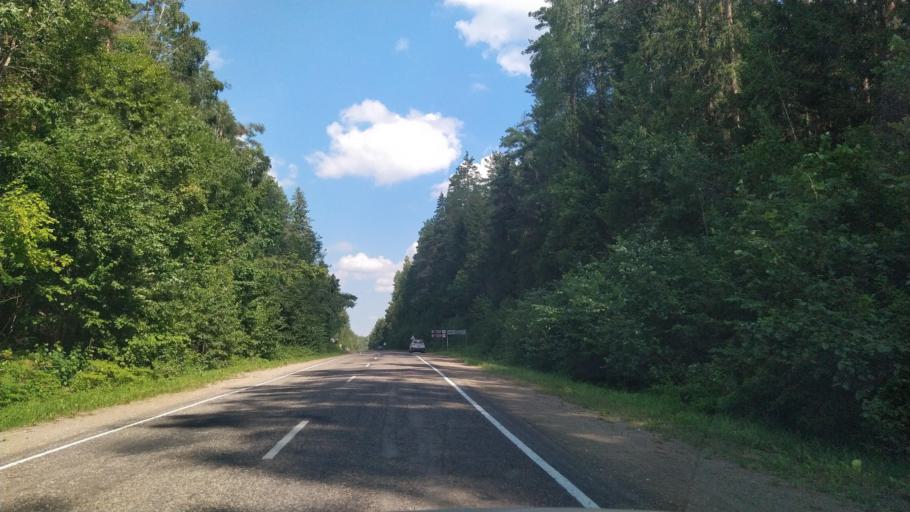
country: RU
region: Pskov
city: Pushkinskiye Gory
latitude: 57.0554
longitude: 28.9448
